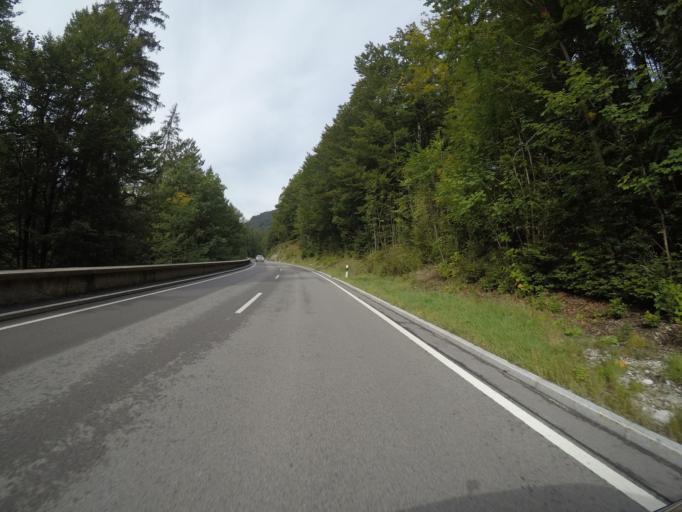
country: DE
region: Bavaria
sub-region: Upper Bavaria
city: Lenggries
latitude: 47.5834
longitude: 11.6072
